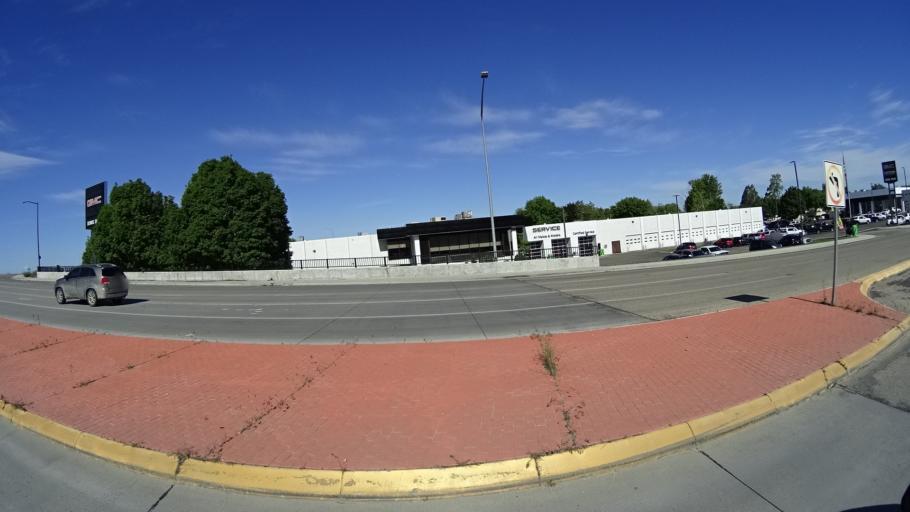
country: US
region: Idaho
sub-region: Ada County
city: Garden City
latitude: 43.5771
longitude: -116.2434
